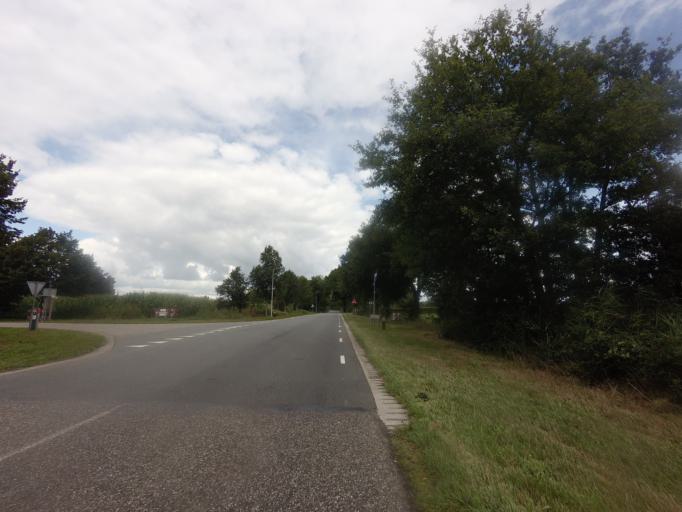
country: NL
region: Drenthe
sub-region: Gemeente Meppel
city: Meppel
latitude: 52.6834
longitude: 6.2141
